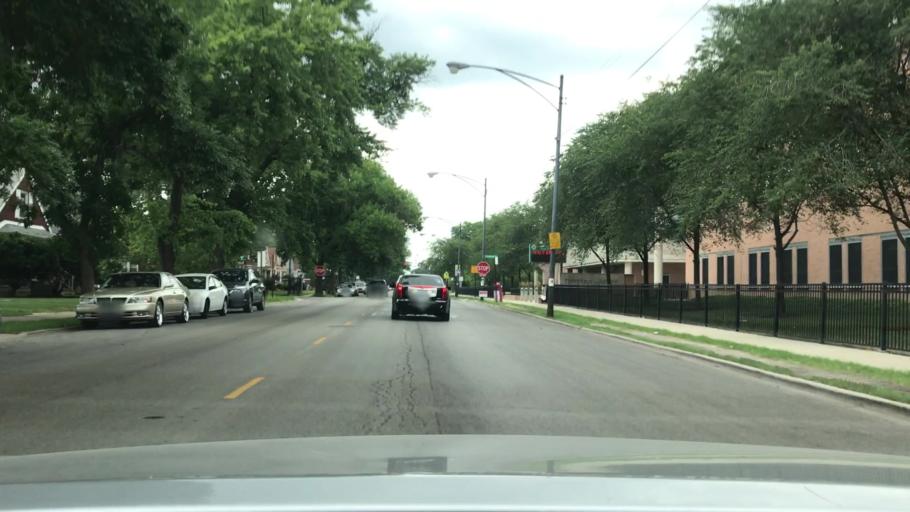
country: US
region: Illinois
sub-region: Cook County
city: Hometown
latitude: 41.7643
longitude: -87.7056
